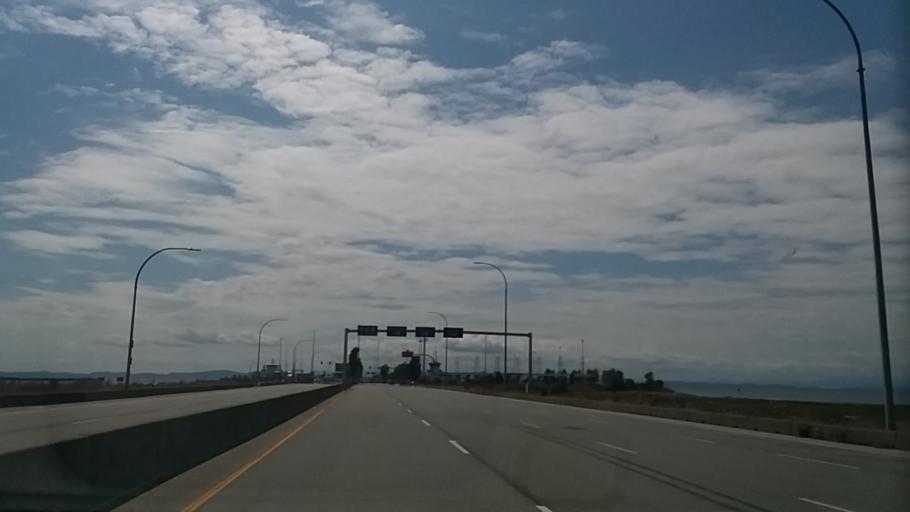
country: US
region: Washington
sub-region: Whatcom County
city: Point Roberts
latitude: 49.0134
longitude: -123.1203
